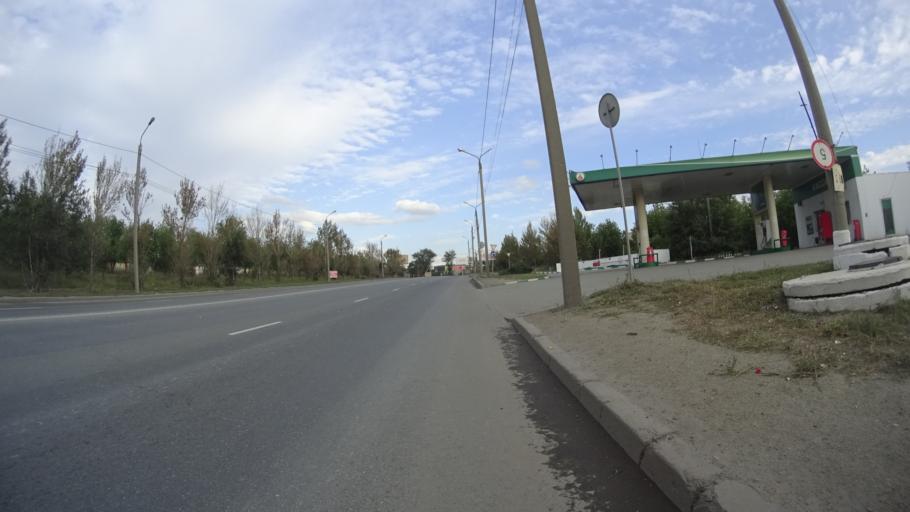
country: RU
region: Chelyabinsk
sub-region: Gorod Chelyabinsk
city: Chelyabinsk
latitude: 55.1926
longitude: 61.4215
